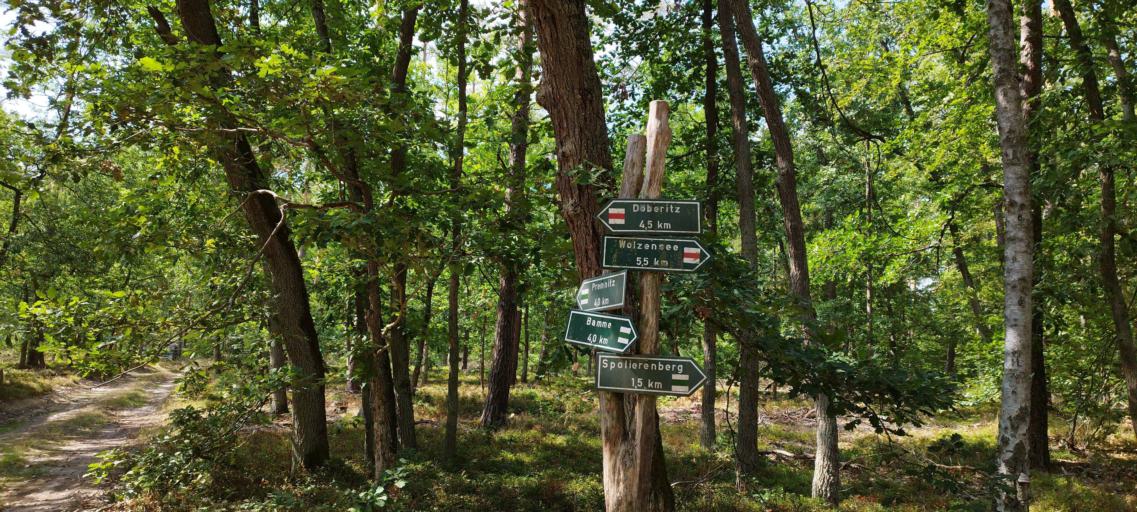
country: DE
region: Brandenburg
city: Premnitz
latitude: 52.5542
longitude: 12.4064
